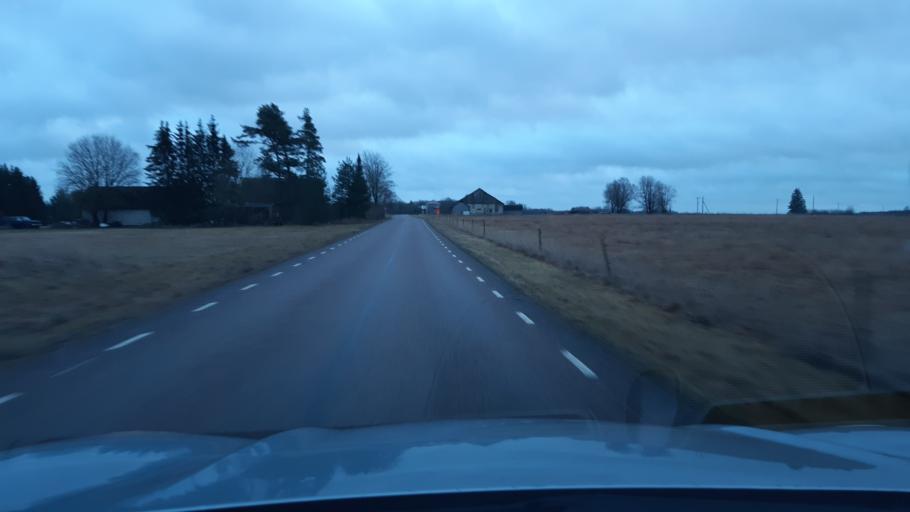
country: EE
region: Raplamaa
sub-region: Rapla vald
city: Rapla
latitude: 59.0173
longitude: 24.6977
